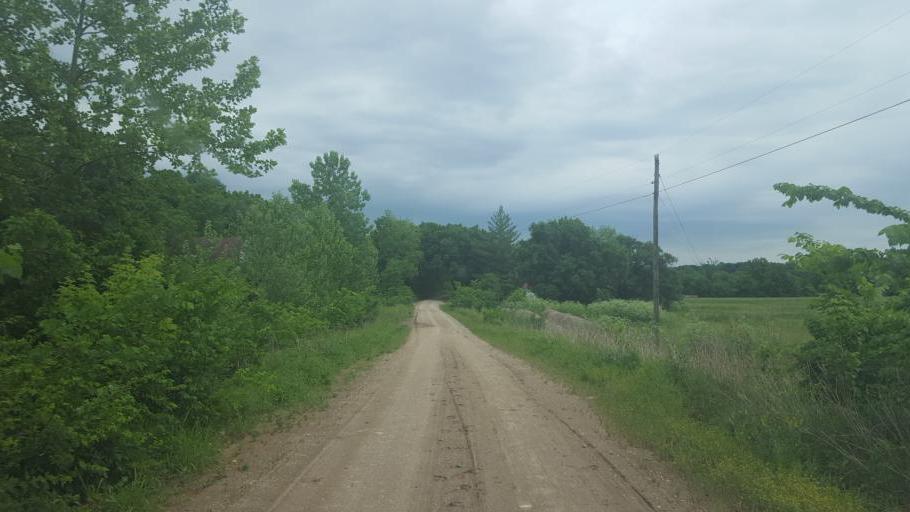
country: US
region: Missouri
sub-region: Moniteau County
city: California
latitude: 38.7351
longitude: -92.6182
